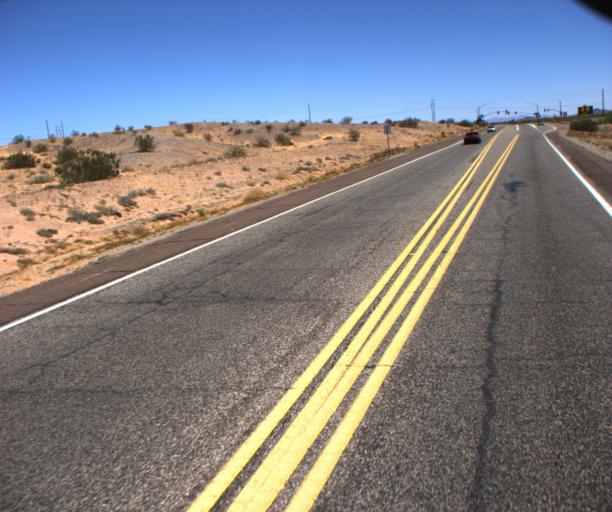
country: US
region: Arizona
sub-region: La Paz County
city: Parker
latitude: 33.9958
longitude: -114.2201
